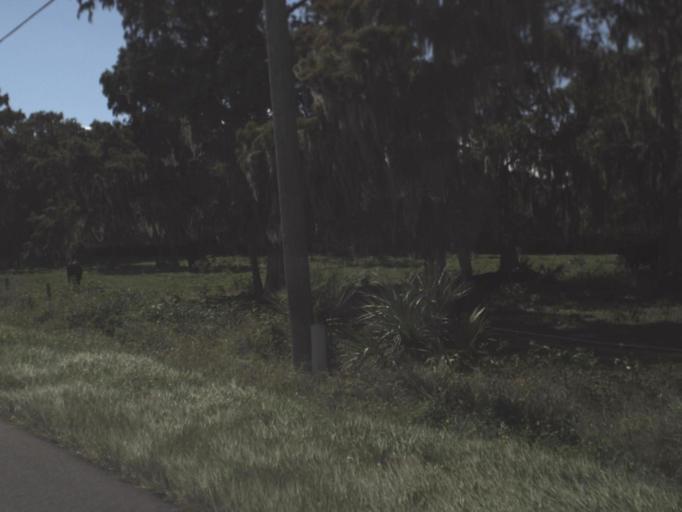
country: US
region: Florida
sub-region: Glades County
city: Buckhead Ridge
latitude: 27.1766
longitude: -80.8551
